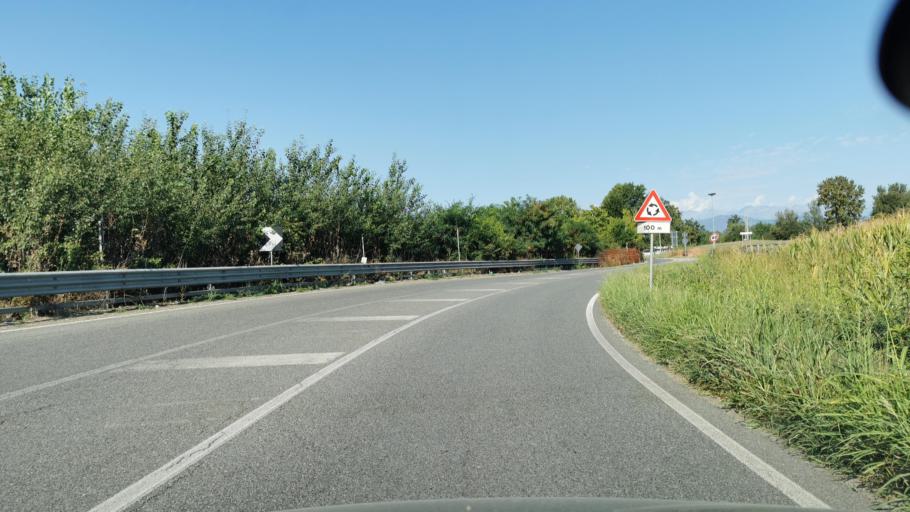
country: IT
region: Piedmont
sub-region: Provincia di Torino
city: Settimo Torinese
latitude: 45.1584
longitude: 7.7550
